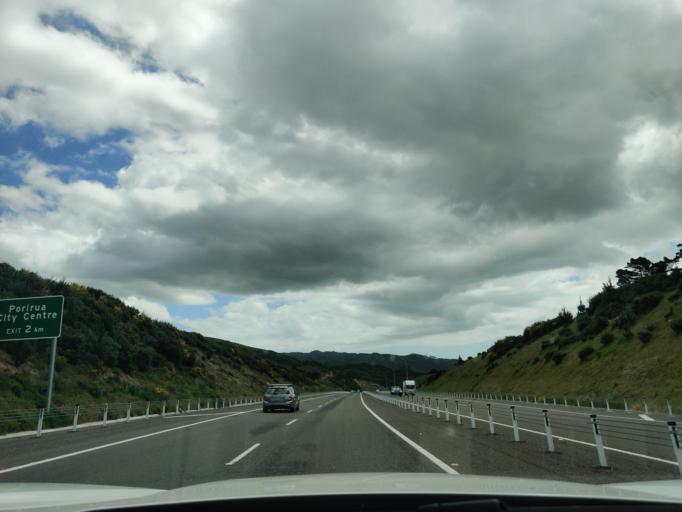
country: NZ
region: Wellington
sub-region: Porirua City
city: Porirua
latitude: -41.1555
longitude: 174.8690
